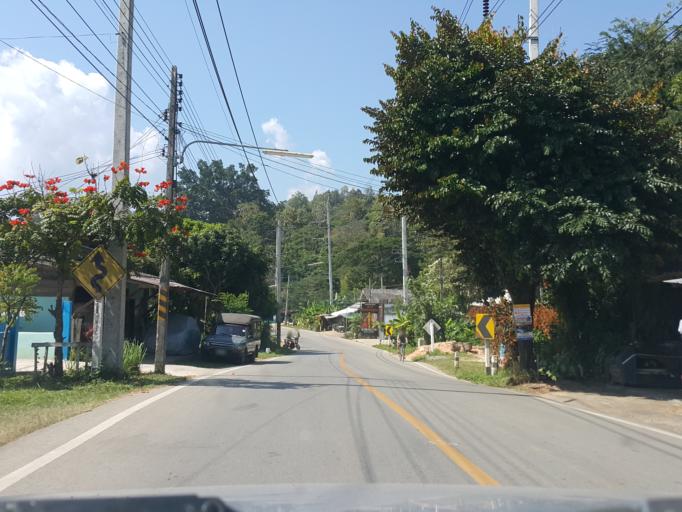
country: TH
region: Chiang Mai
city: Mae Taeng
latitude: 19.1077
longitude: 98.8294
